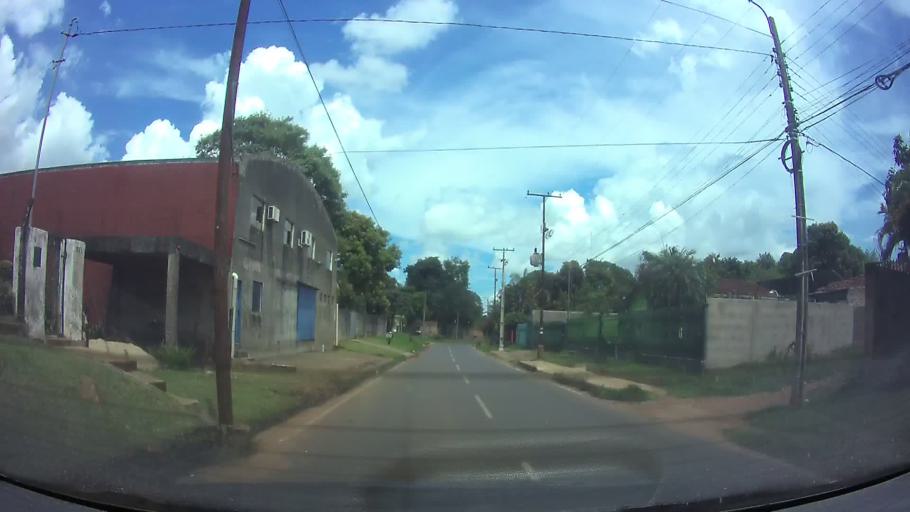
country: PY
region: Central
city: San Lorenzo
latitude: -25.3009
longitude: -57.4988
